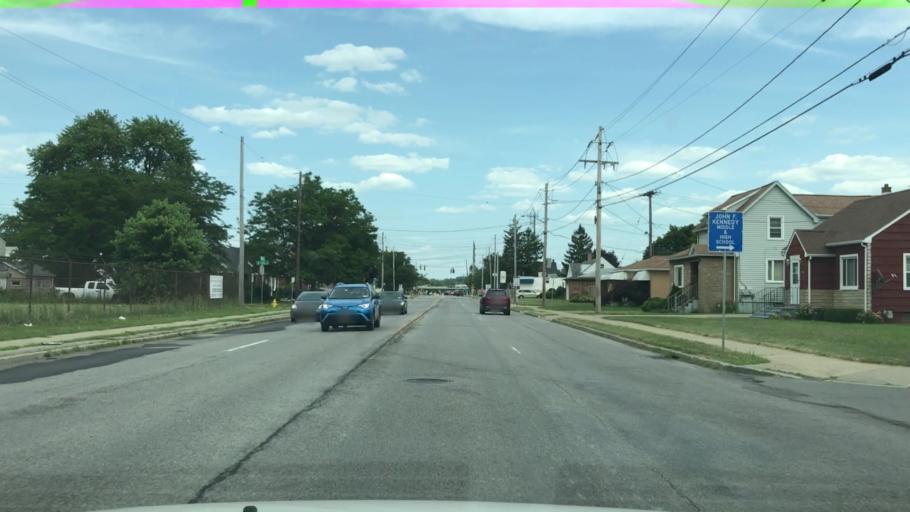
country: US
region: New York
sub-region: Erie County
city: Sloan
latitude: 42.8842
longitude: -78.7742
